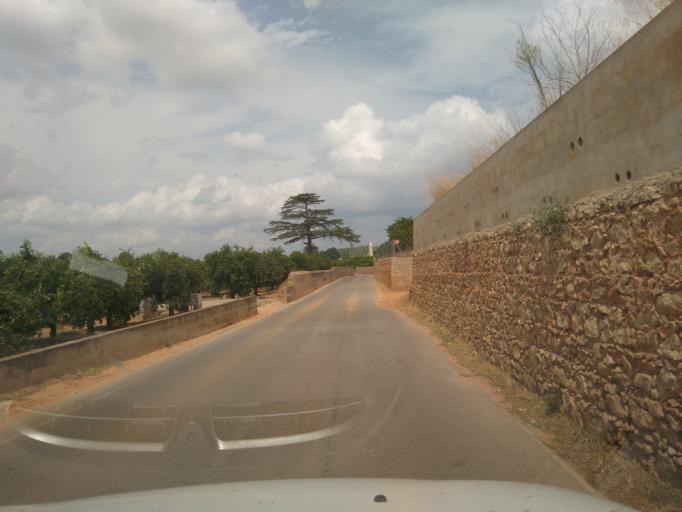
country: ES
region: Valencia
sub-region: Provincia de Valencia
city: La Pobla Llarga
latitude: 39.0975
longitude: -0.4319
